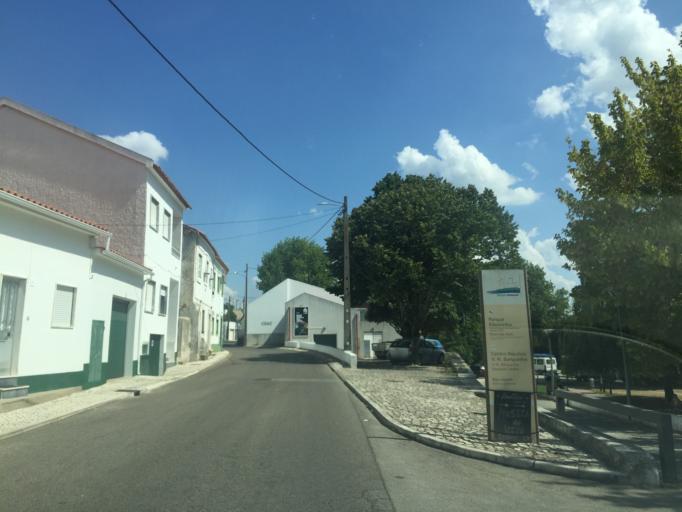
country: PT
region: Santarem
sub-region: Chamusca
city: Vila Nova da Barquinha
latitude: 39.4578
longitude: -8.4267
